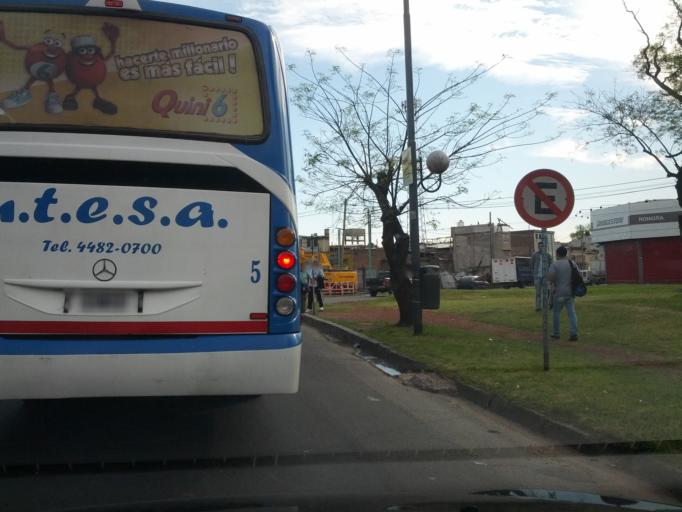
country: AR
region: Buenos Aires
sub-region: Partido de Avellaneda
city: Avellaneda
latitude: -34.6472
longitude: -58.4029
